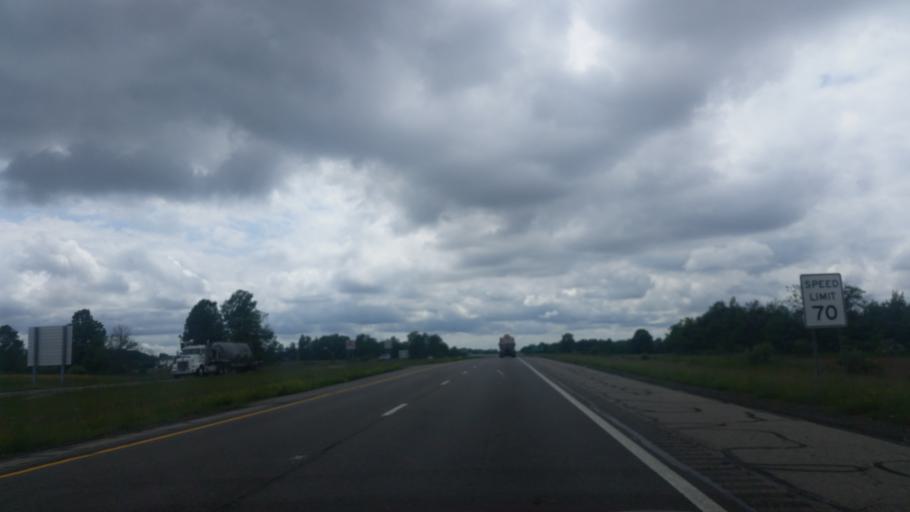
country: US
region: Ohio
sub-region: Crawford County
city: Crestline
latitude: 40.7737
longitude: -82.6704
